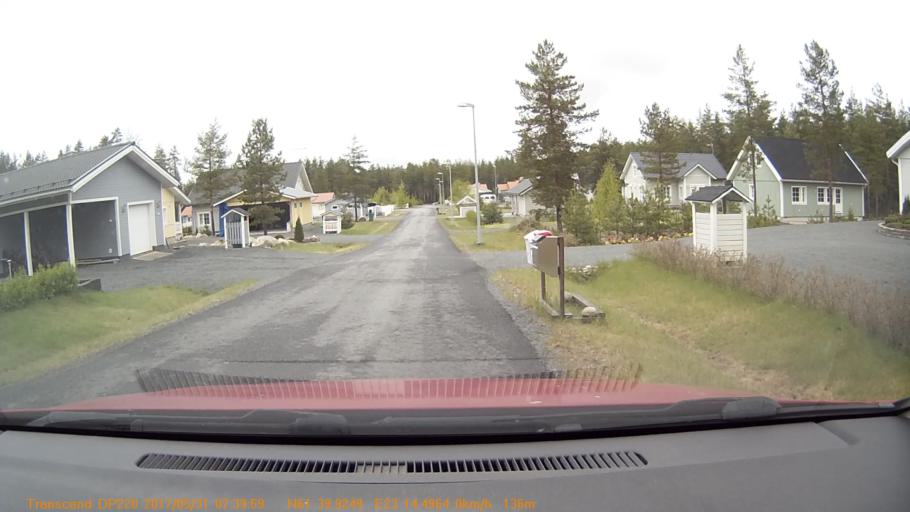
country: FI
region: Pirkanmaa
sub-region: Tampere
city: Viljakkala
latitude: 61.6654
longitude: 23.2416
